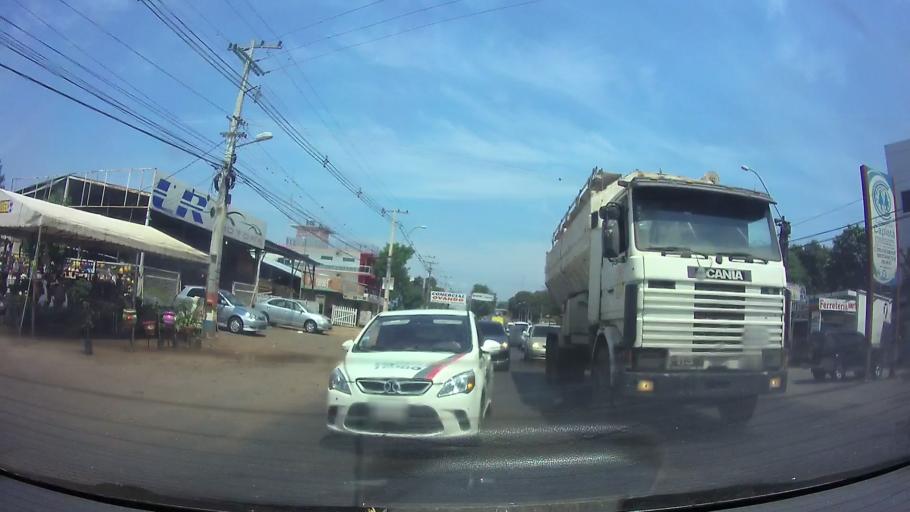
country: PY
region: Central
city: Capiata
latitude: -25.3926
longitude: -57.4685
